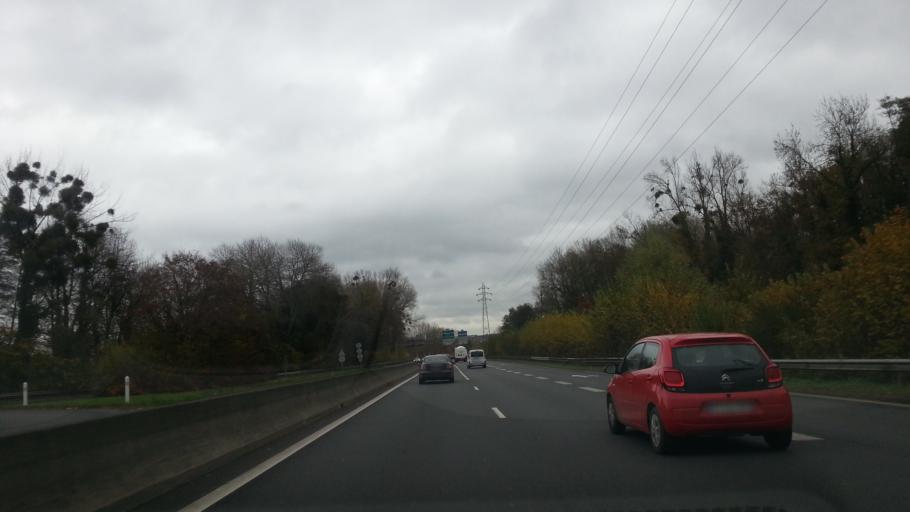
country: FR
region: Picardie
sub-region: Departement de l'Oise
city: Monchy-Saint-Eloi
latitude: 49.2861
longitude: 2.4708
